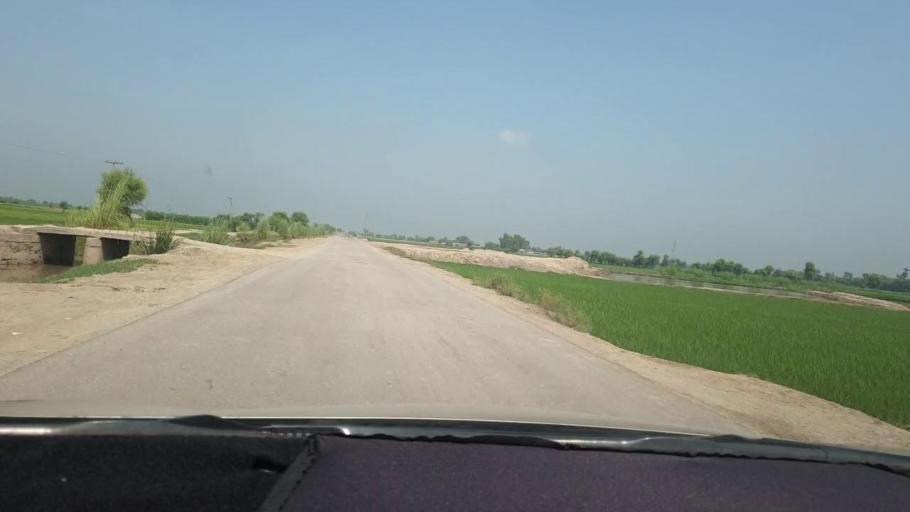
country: PK
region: Sindh
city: Miro Khan
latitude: 27.7745
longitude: 68.0579
